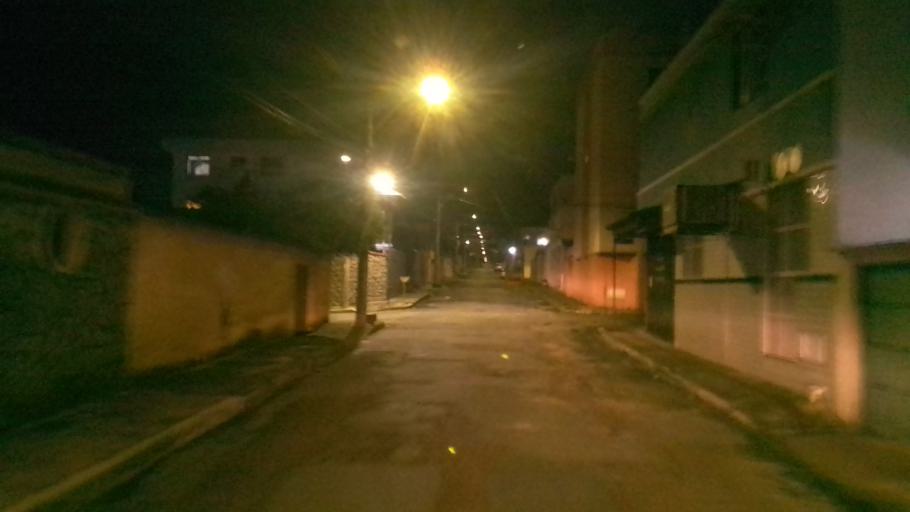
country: BR
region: Minas Gerais
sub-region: Belo Horizonte
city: Belo Horizonte
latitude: -19.8855
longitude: -43.9387
